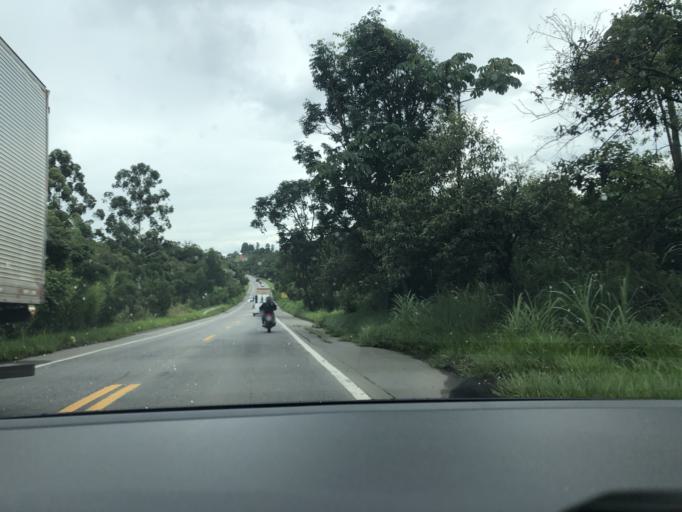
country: BR
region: Sao Paulo
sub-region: Jarinu
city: Jarinu
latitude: -23.1390
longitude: -46.7417
